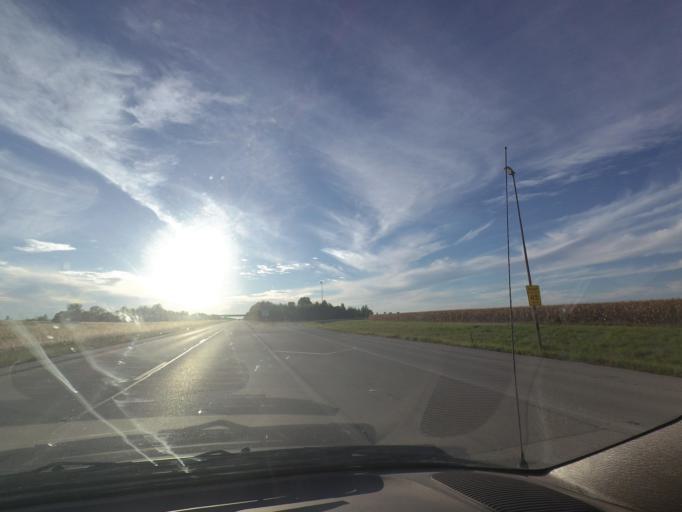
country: US
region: Illinois
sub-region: Sangamon County
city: New Berlin
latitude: 39.7404
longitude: -89.9184
